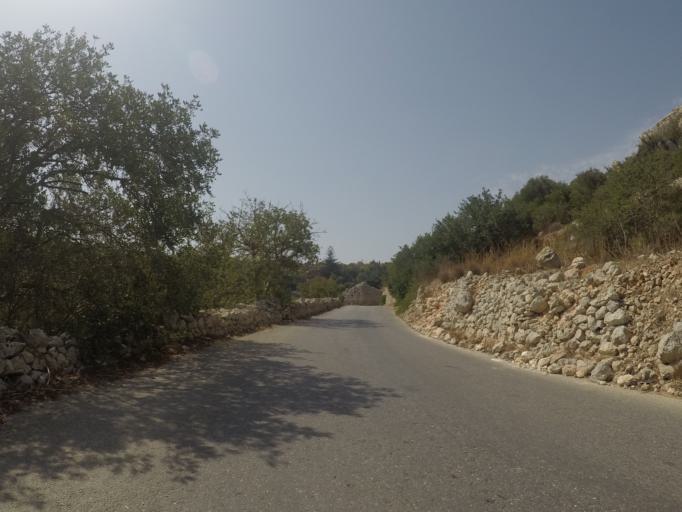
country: MT
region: L-Imgarr
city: Imgarr
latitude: 35.9369
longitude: 14.3803
